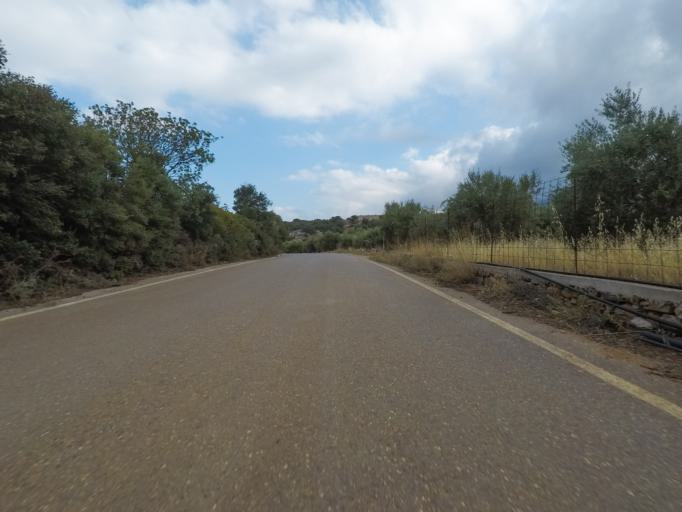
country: GR
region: Crete
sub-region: Nomos Lasithiou
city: Kritsa
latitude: 35.1718
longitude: 25.6535
